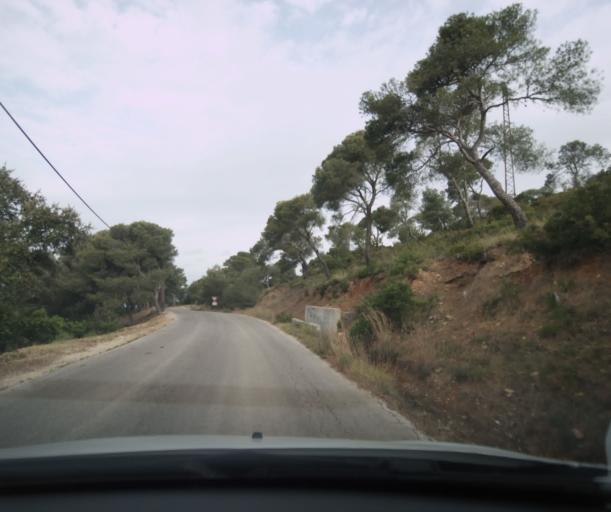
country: FR
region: Provence-Alpes-Cote d'Azur
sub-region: Departement du Var
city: Le Pradet
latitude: 43.0834
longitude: 6.0262
